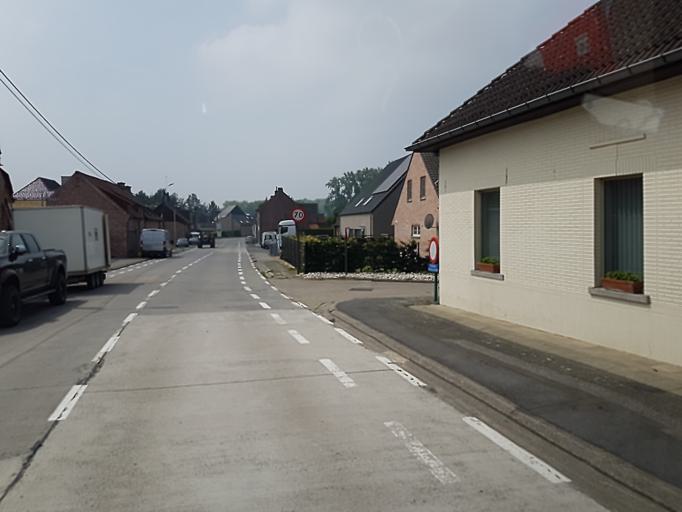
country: BE
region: Flanders
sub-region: Provincie Oost-Vlaanderen
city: Sint-Maria-Lierde
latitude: 50.8170
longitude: 3.8832
